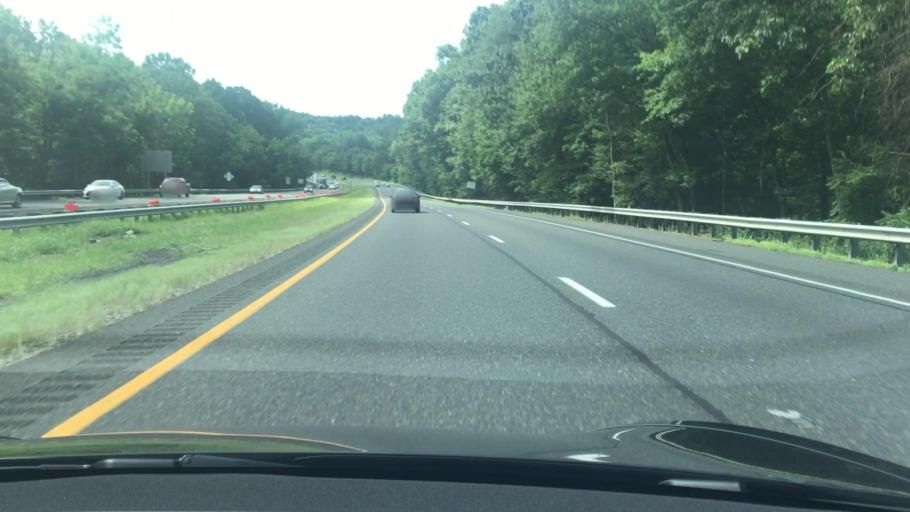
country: US
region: Maryland
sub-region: Baltimore County
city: Hunt Valley
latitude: 39.5837
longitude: -76.6775
